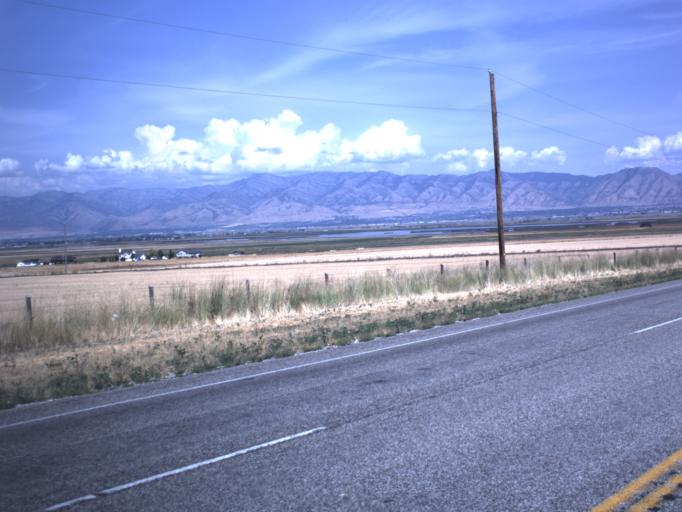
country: US
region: Utah
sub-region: Cache County
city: Mendon
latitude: 41.7535
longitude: -111.9910
